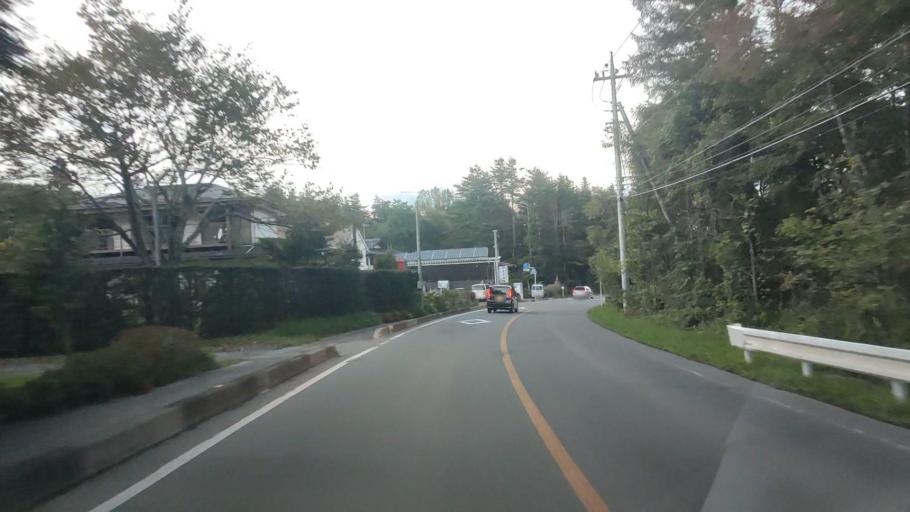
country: JP
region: Nagano
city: Komoro
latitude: 36.4876
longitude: 138.5823
